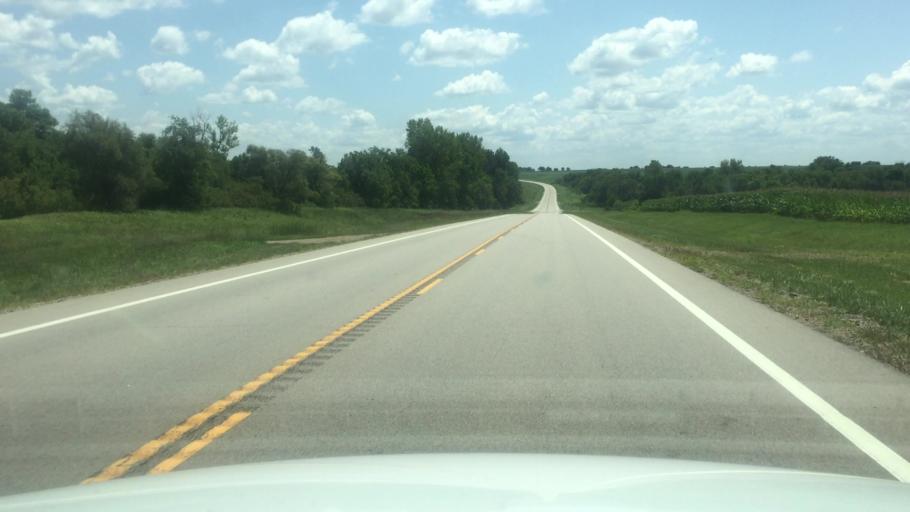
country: US
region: Kansas
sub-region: Brown County
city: Horton
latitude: 39.6263
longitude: -95.3507
